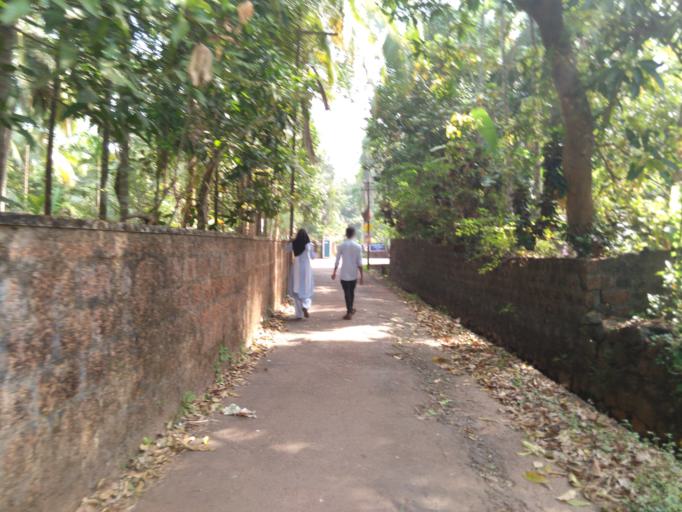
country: IN
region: Kerala
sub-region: Kozhikode
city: Kunnamangalam
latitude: 11.2886
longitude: 75.8353
